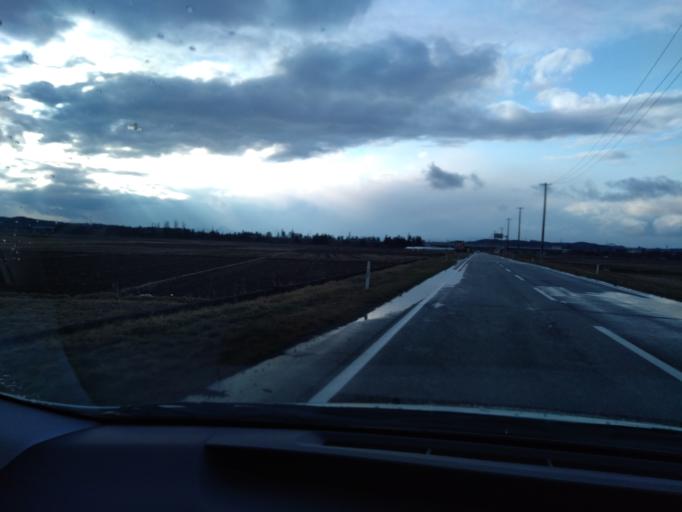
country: JP
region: Iwate
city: Ichinoseki
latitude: 38.7929
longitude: 141.0930
